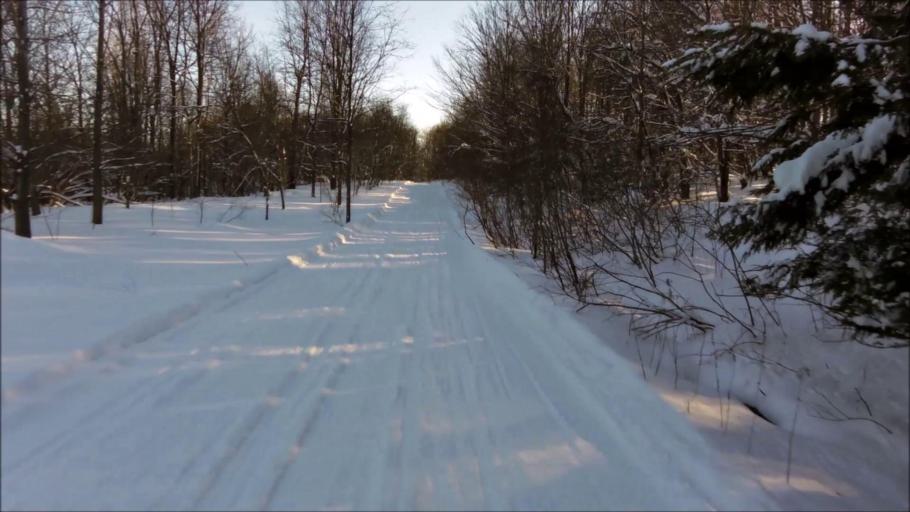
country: US
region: New York
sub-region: Chautauqua County
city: Mayville
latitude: 42.2543
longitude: -79.3867
